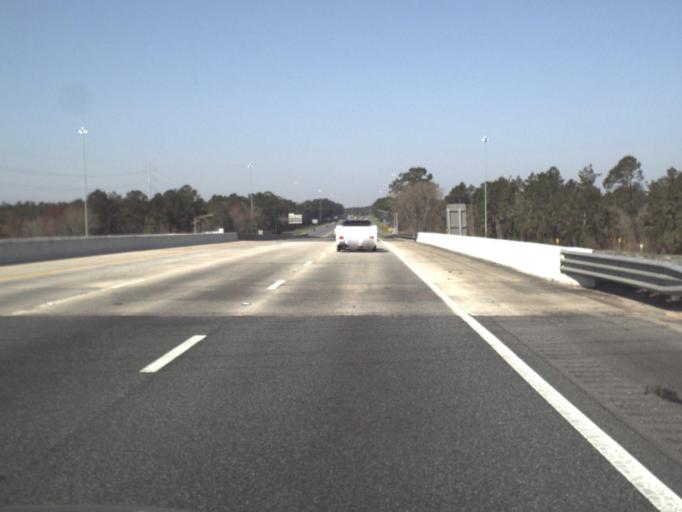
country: US
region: Florida
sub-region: Leon County
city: Tallahassee
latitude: 30.4796
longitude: -84.3626
